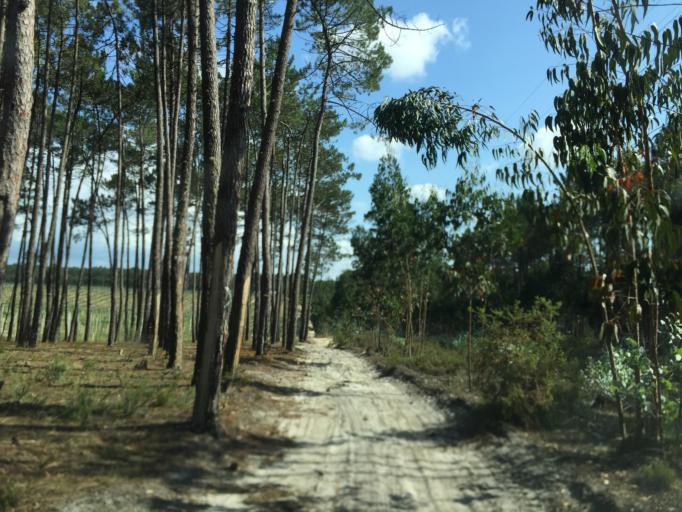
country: PT
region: Leiria
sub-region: Leiria
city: Monte Redondo
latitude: 39.9477
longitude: -8.8257
